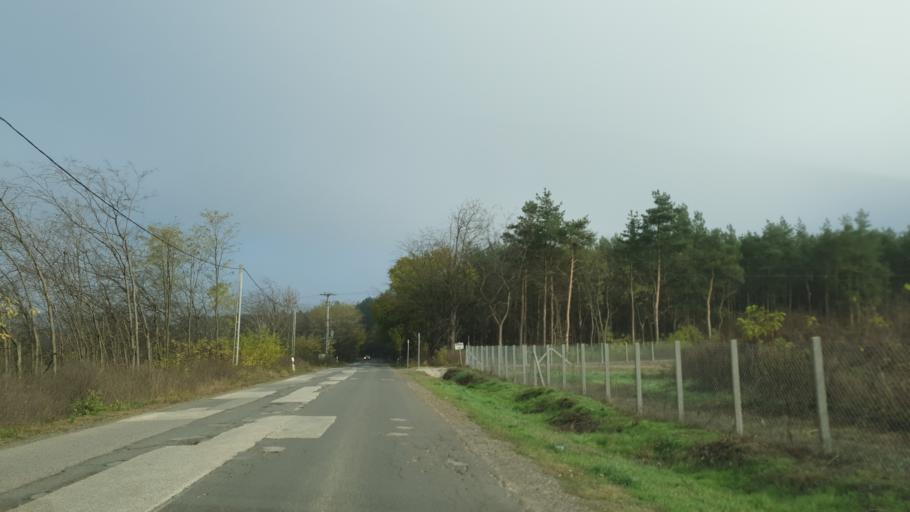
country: HU
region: Pest
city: Orbottyan
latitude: 47.6731
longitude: 19.2517
